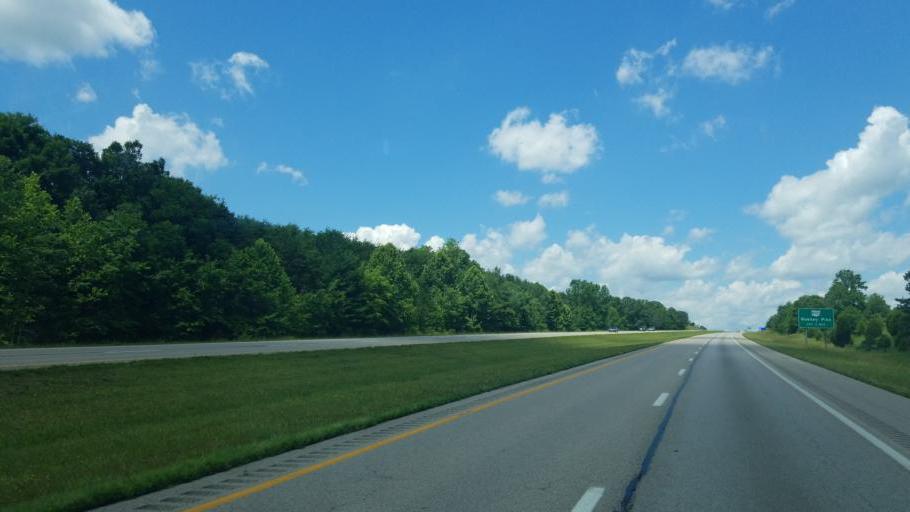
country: US
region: Ohio
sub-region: Gallia County
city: Gallipolis
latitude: 38.8701
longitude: -82.2765
